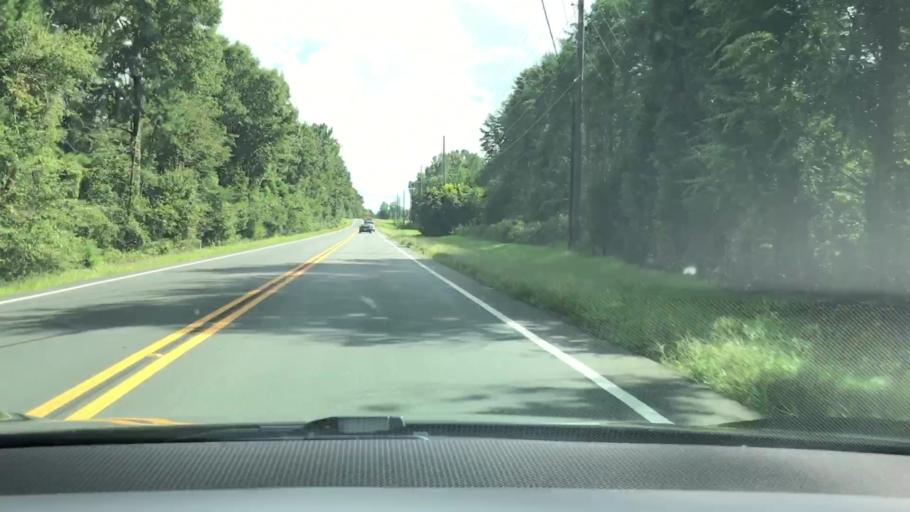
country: US
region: Alabama
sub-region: Montgomery County
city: Pike Road
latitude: 32.3357
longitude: -86.0947
